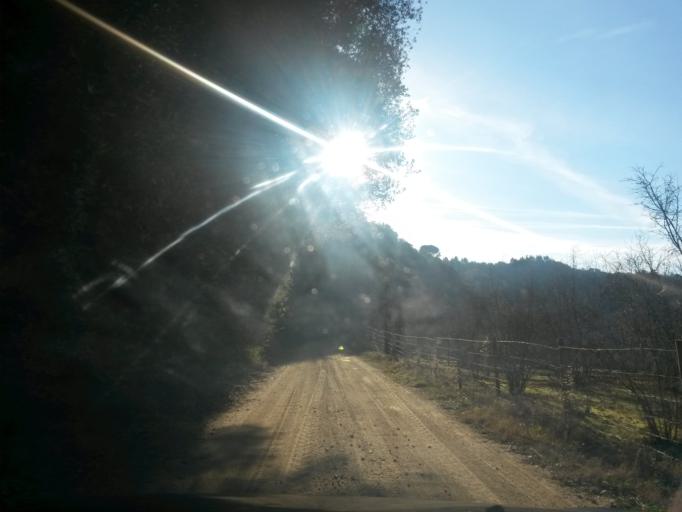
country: ES
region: Catalonia
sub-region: Provincia de Girona
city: la Cellera de Ter
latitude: 41.9813
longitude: 2.6296
